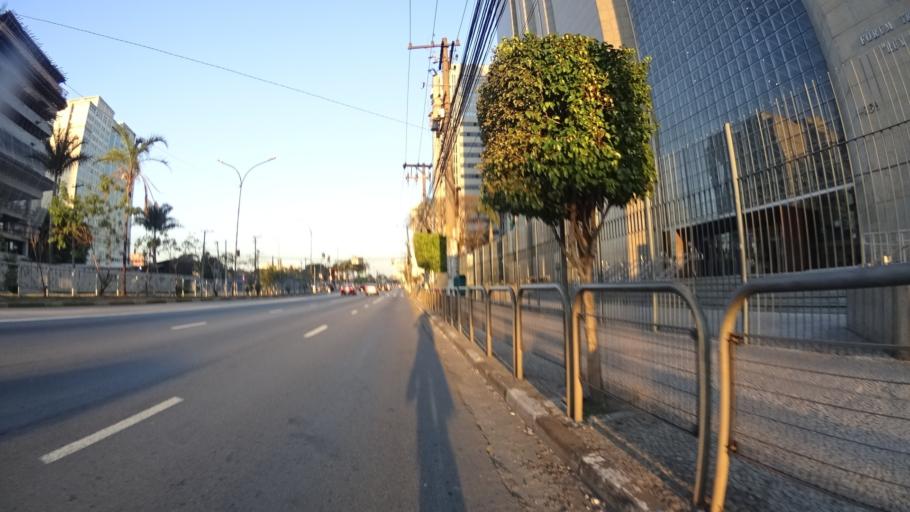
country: BR
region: Sao Paulo
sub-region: Sao Paulo
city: Sao Paulo
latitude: -23.5224
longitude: -46.6619
